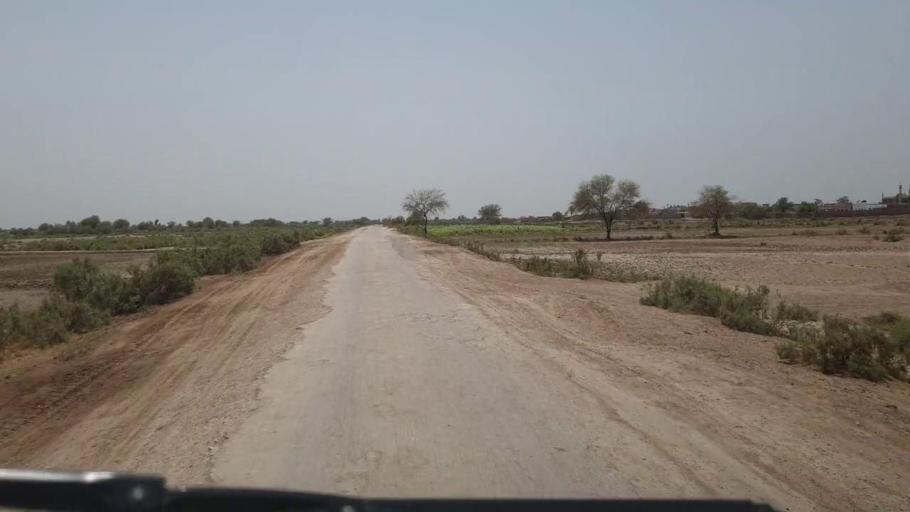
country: PK
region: Sindh
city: Daulatpur
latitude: 26.4620
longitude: 68.1294
